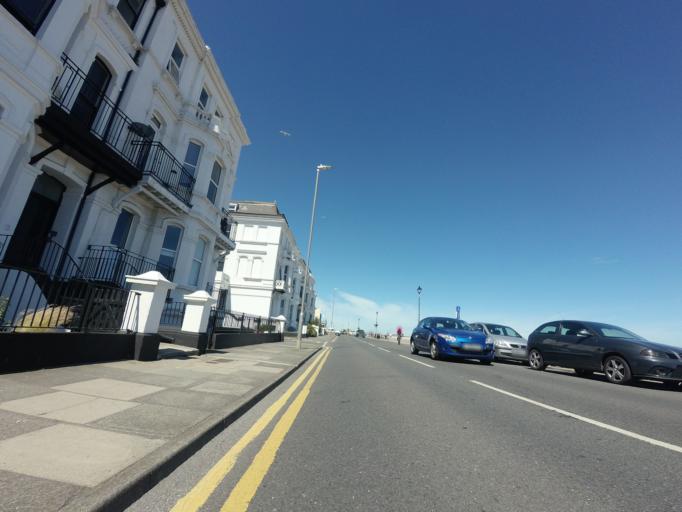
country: GB
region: England
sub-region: Kent
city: Deal
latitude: 51.2211
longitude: 1.4046
